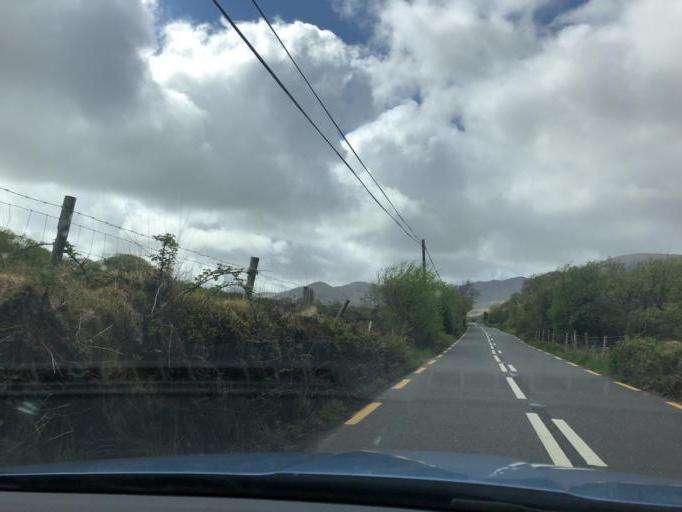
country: IE
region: Munster
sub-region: Ciarrai
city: Cahersiveen
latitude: 51.8297
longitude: -9.9395
